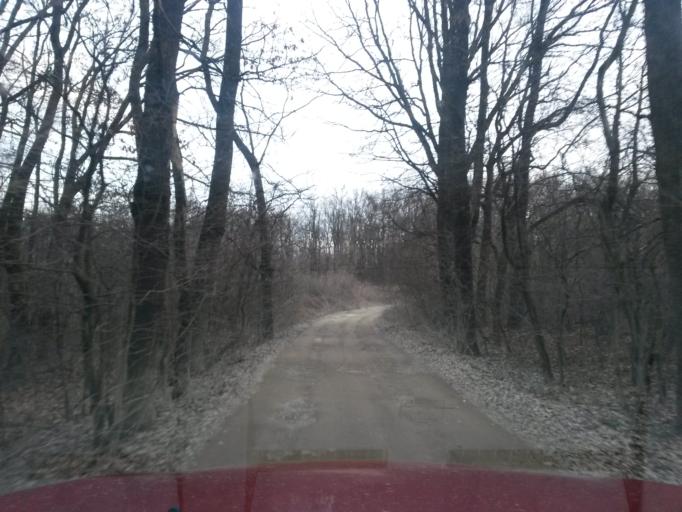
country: SK
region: Kosicky
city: Kosice
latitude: 48.7064
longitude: 21.2950
